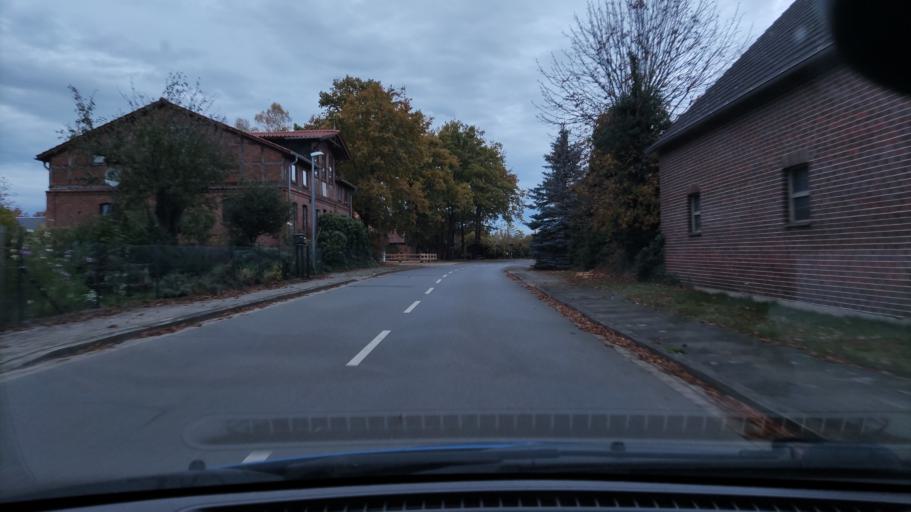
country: DE
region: Lower Saxony
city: Prezelle
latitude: 52.9189
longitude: 11.3569
